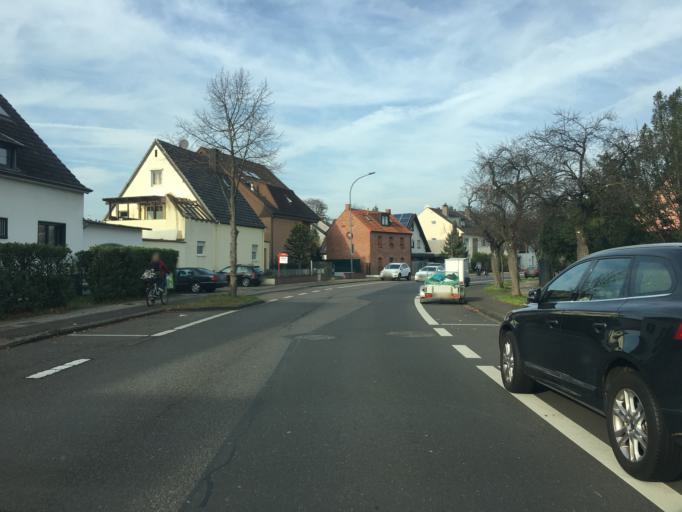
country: DE
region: North Rhine-Westphalia
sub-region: Regierungsbezirk Koln
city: Rath
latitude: 50.9500
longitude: 7.1027
